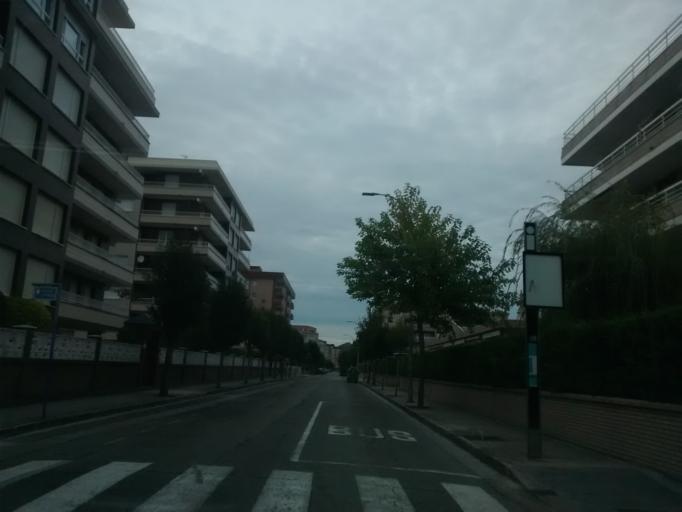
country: ES
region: Cantabria
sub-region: Provincia de Cantabria
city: Colindres
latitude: 43.4167
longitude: -3.4410
